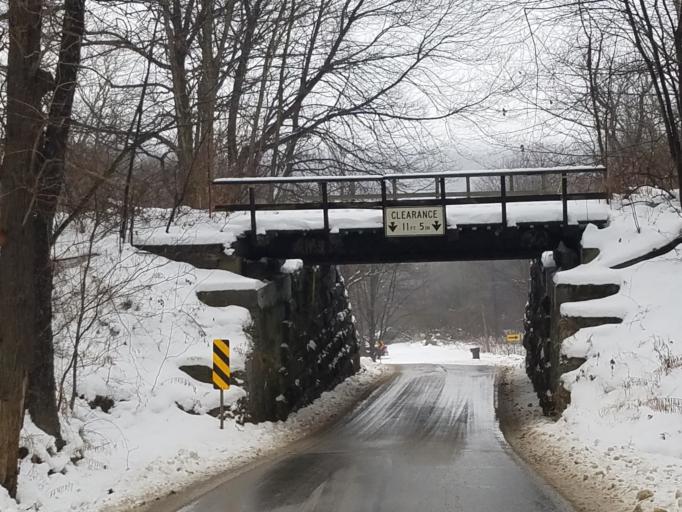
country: US
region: Pennsylvania
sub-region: Mercer County
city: Greenville
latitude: 41.3803
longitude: -80.3577
